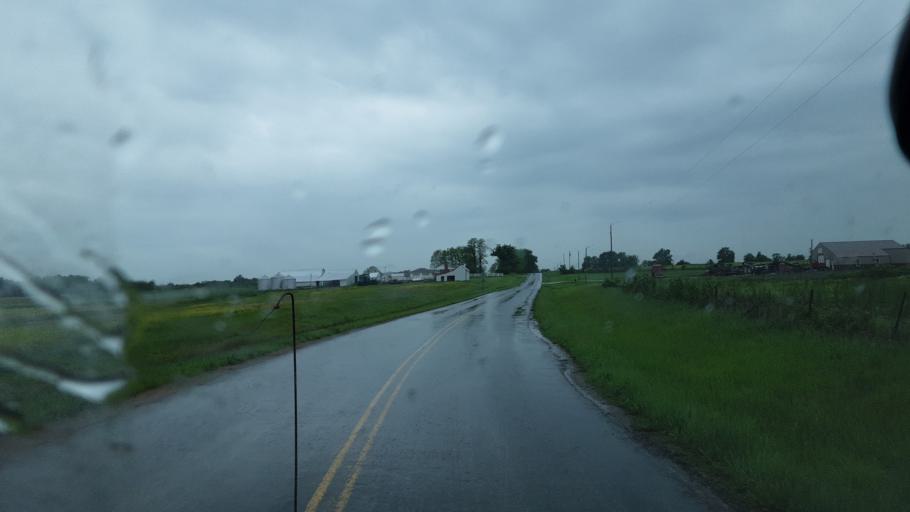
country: US
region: Missouri
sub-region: Boone County
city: Centralia
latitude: 39.3678
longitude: -92.2506
